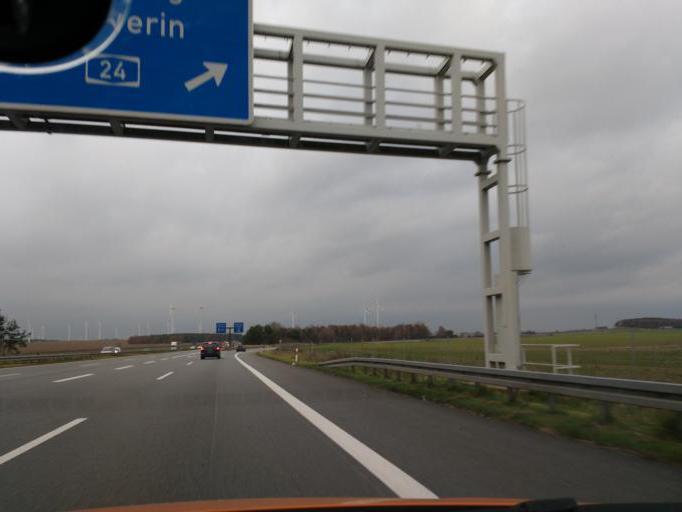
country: DE
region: Brandenburg
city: Wittstock
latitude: 53.1225
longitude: 12.4630
